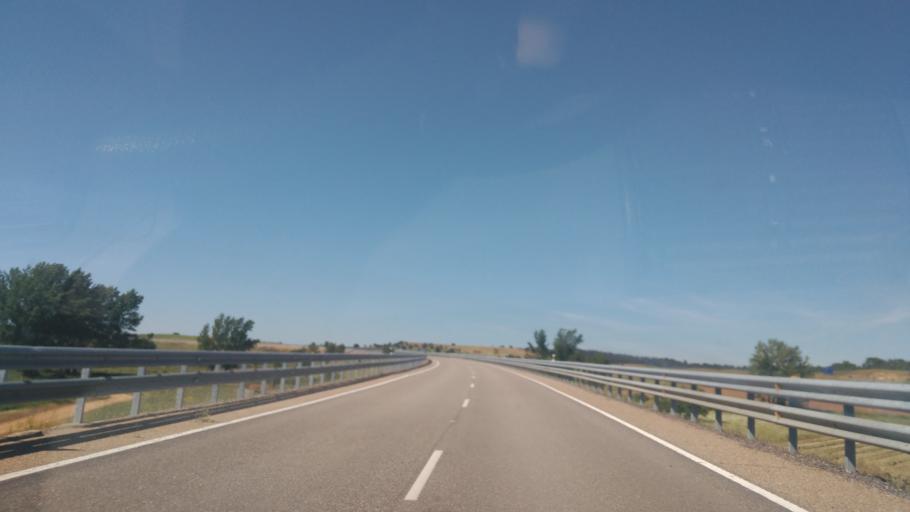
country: ES
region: Castille and Leon
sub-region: Provincia de Zamora
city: Cuelgamures
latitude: 41.2524
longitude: -5.7035
